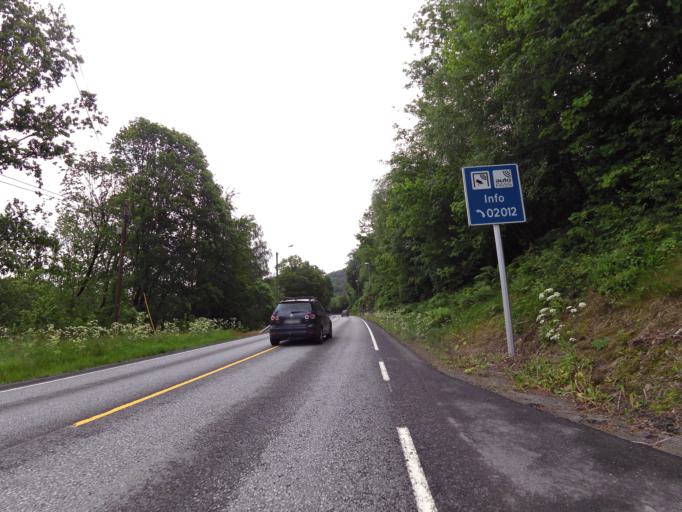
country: NO
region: Vest-Agder
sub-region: Lyngdal
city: Lyngdal
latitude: 58.1130
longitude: 6.9452
